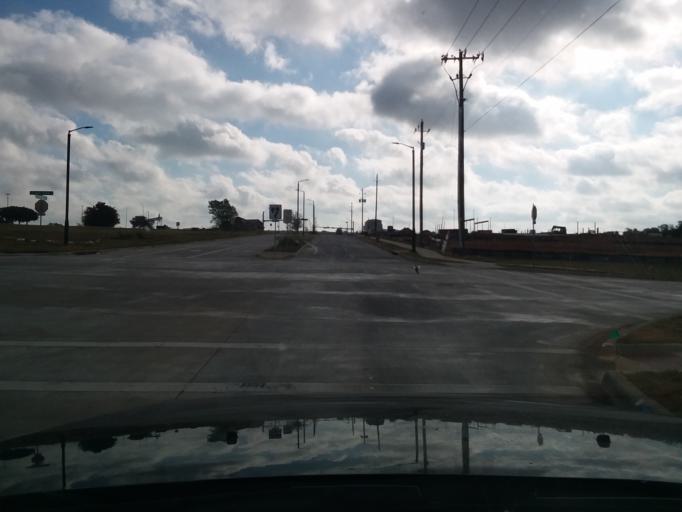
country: US
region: Texas
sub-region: Denton County
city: Hickory Creek
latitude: 33.1226
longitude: -97.0389
